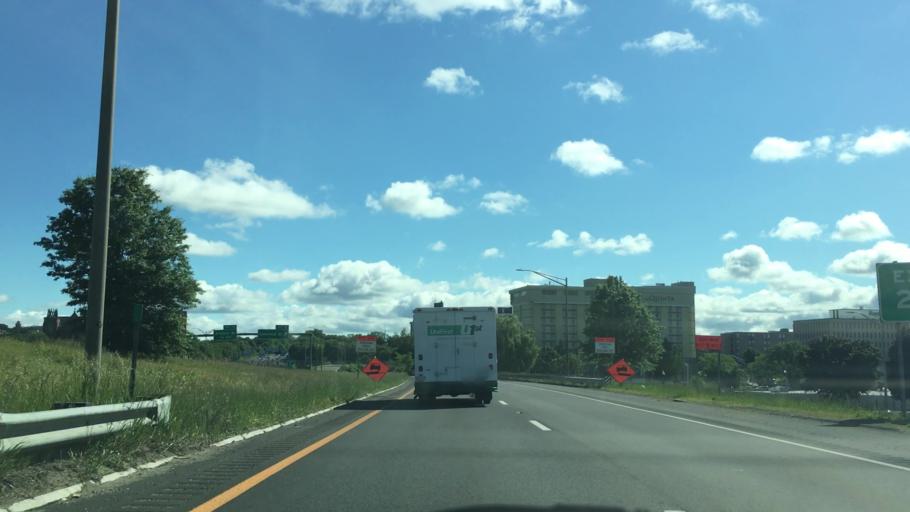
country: US
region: Massachusetts
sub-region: Hampden County
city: Springfield
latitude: 42.1083
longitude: -72.5986
